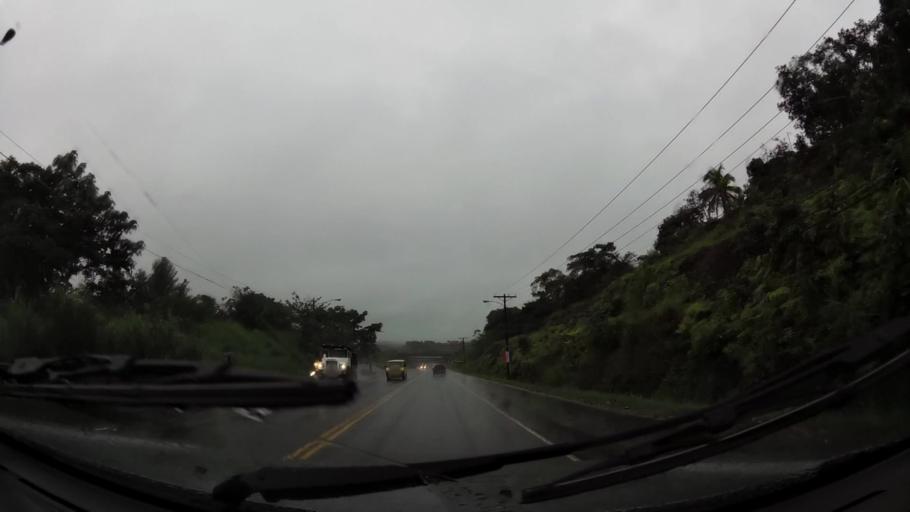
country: PA
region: Colon
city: Santa Rita Arriba
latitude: 9.3192
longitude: -79.7967
